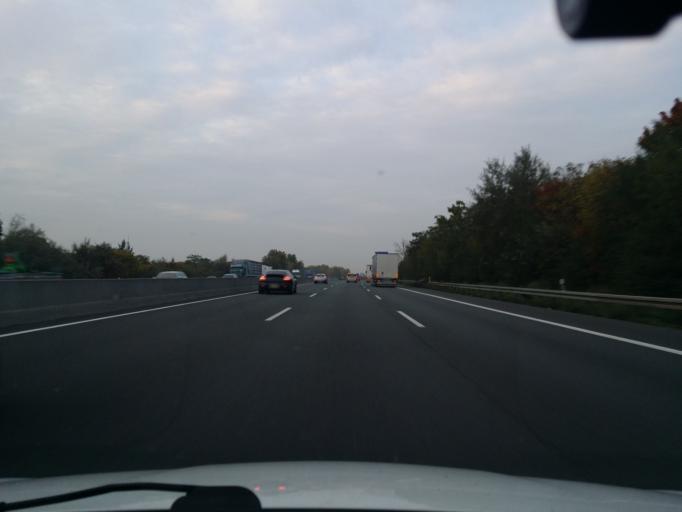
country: DE
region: Hesse
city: Lorsch
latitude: 49.6538
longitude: 8.5523
